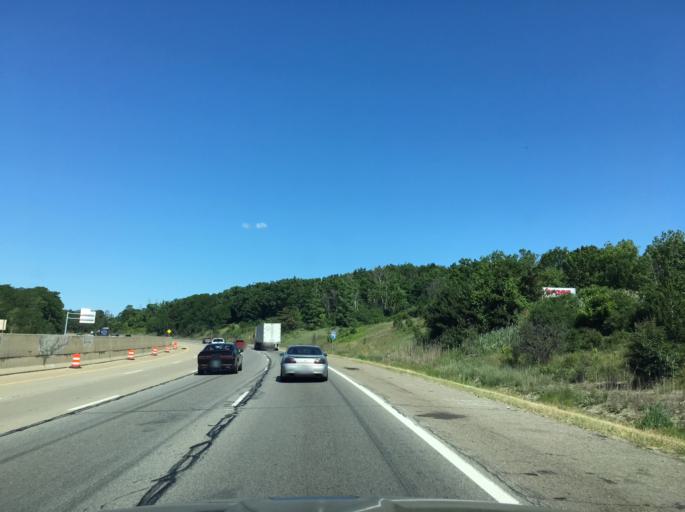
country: US
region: Michigan
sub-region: Oakland County
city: Auburn Hills
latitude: 42.6953
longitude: -83.2545
